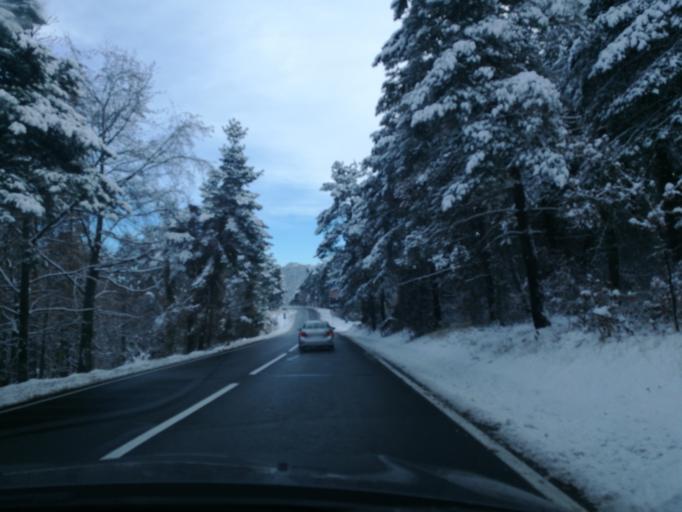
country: RO
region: Brasov
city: Brasov
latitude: 45.6334
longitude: 25.5612
